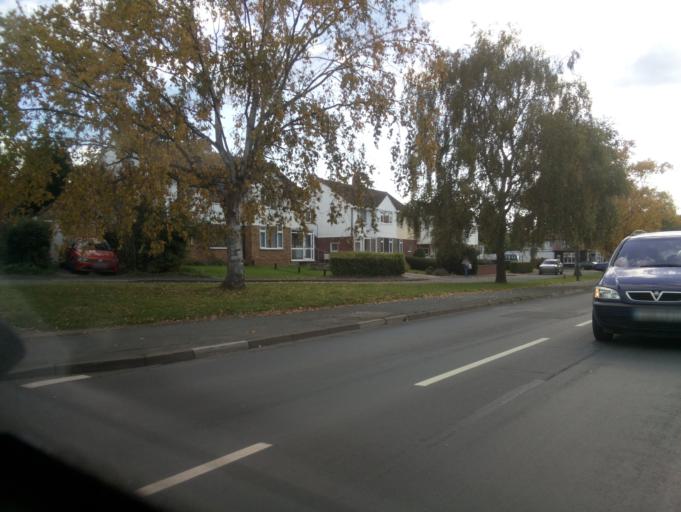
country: GB
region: England
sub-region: Herefordshire
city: Hereford
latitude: 52.0569
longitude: -2.6956
